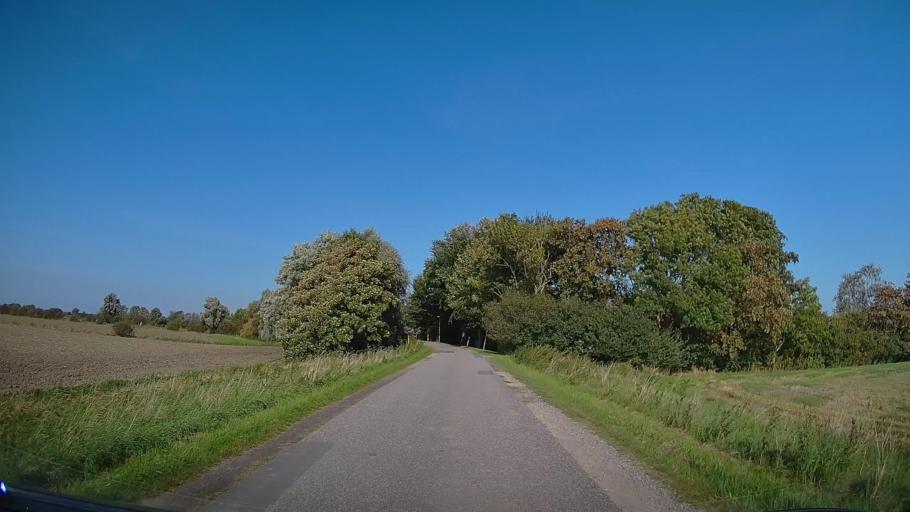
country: DE
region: Lower Saxony
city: Padingbuttel
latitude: 53.7043
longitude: 8.5016
